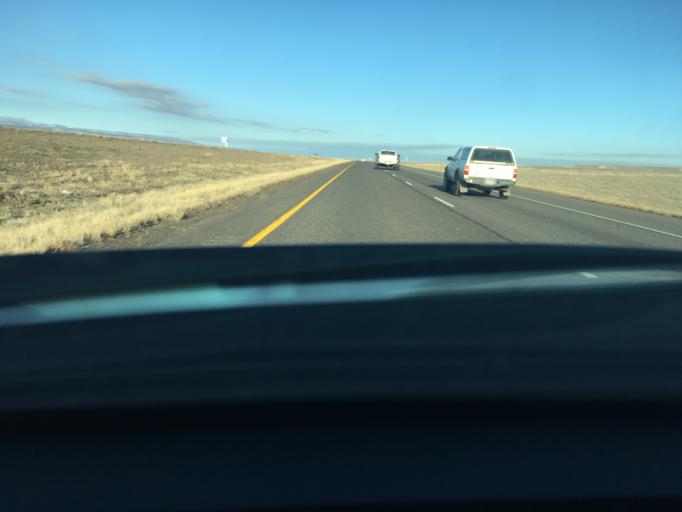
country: US
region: Colorado
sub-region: Delta County
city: Delta
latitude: 38.7869
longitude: -108.2496
